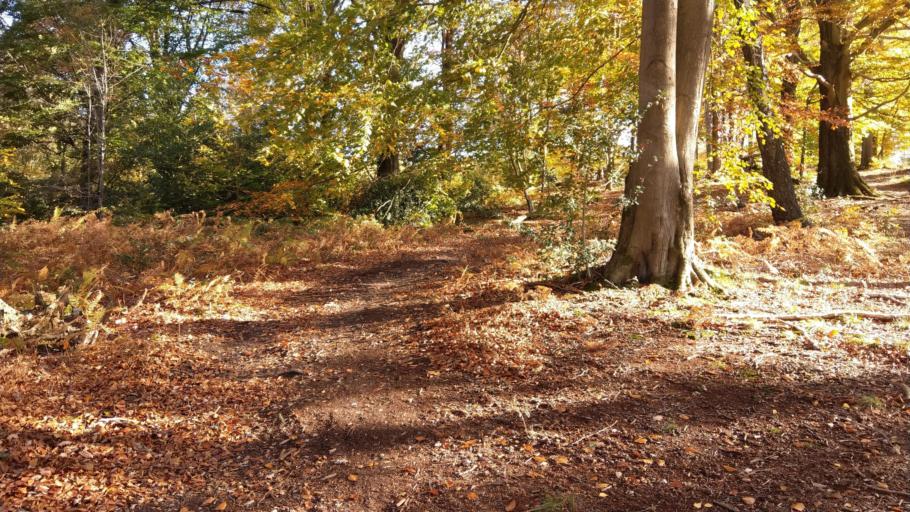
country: NL
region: Limburg
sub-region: Gemeente Vaals
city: Vaals
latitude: 50.7472
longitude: 6.0189
